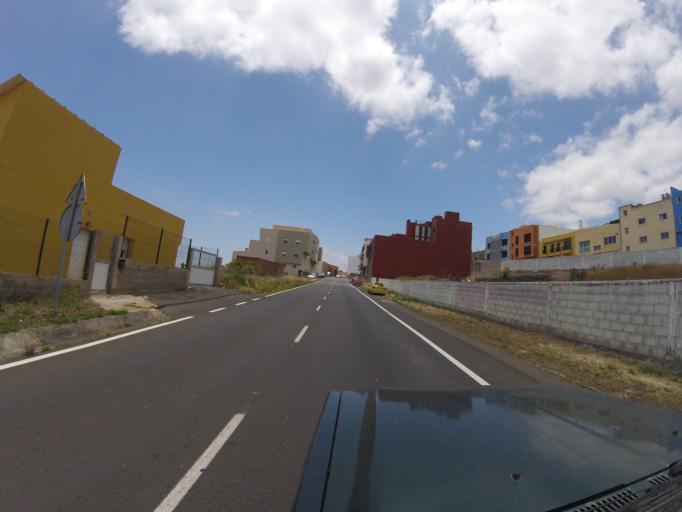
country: ES
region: Canary Islands
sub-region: Provincia de Santa Cruz de Tenerife
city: La Laguna
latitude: 28.4414
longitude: -16.3110
